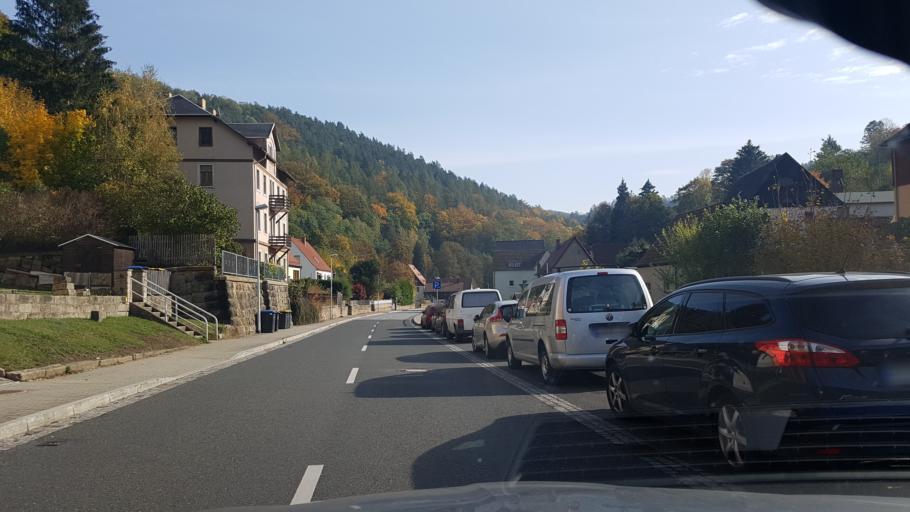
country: DE
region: Saxony
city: Konigstein
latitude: 50.9145
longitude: 14.0600
